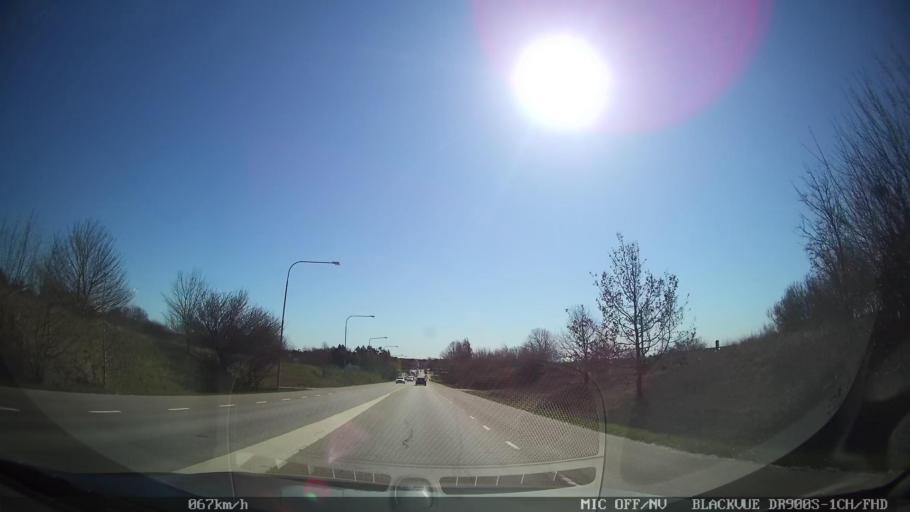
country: SE
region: Skane
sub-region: Ystads Kommun
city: Ystad
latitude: 55.4355
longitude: 13.7974
